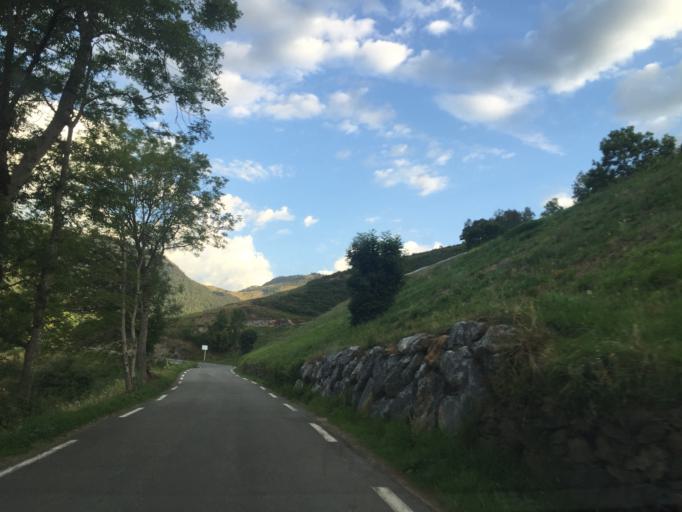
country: FR
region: Midi-Pyrenees
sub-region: Departement des Hautes-Pyrenees
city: Saint-Lary-Soulan
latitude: 42.9220
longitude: 0.3526
